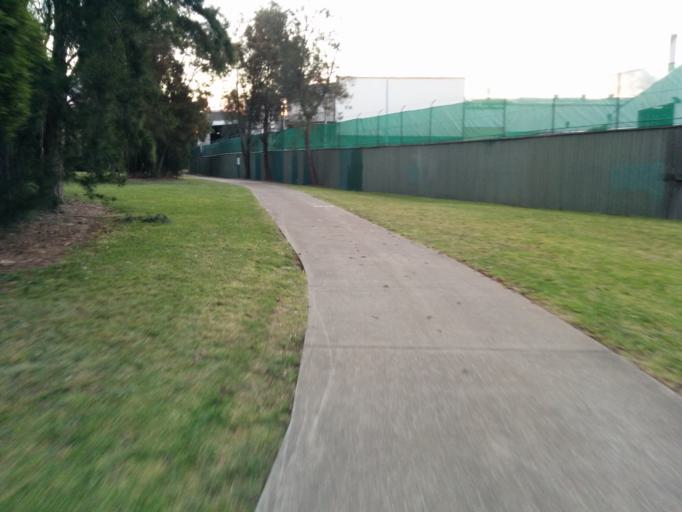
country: AU
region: New South Wales
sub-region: Fairfield
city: Fairfield Heights
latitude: -33.8530
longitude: 150.9523
